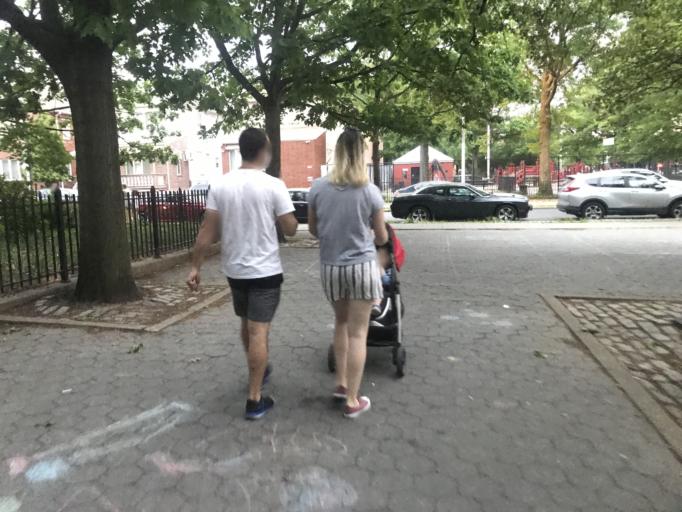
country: US
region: New York
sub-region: Kings County
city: Bensonhurst
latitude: 40.6095
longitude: -73.9996
